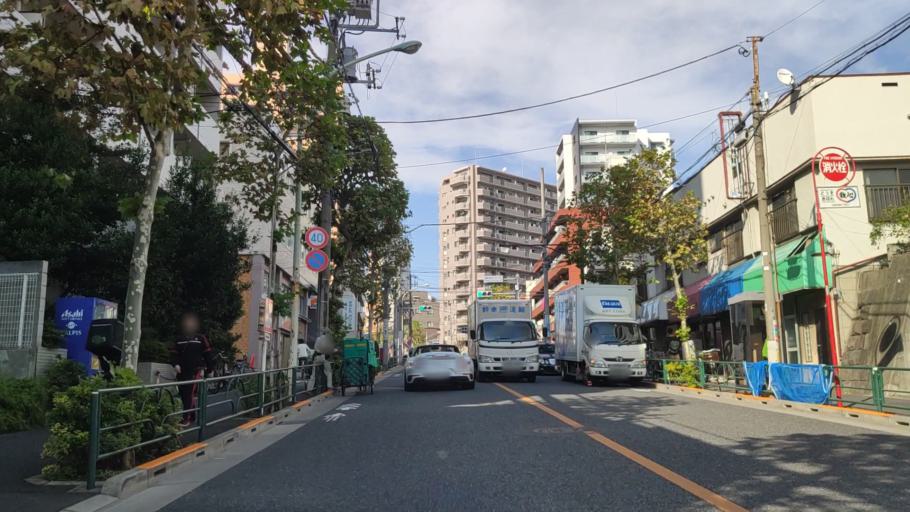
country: JP
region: Tokyo
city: Tokyo
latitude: 35.6933
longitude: 139.6687
